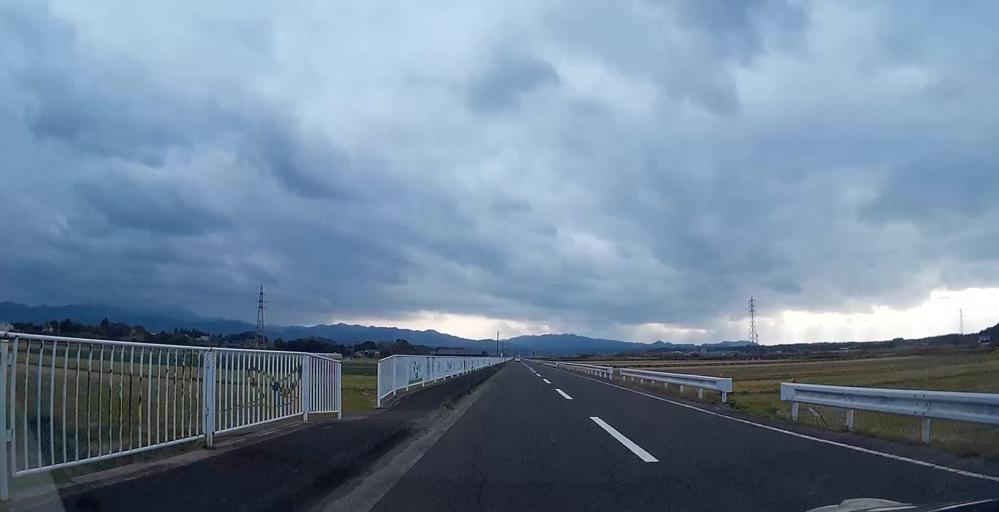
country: JP
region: Kagoshima
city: Izumi
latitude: 32.0903
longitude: 130.2763
